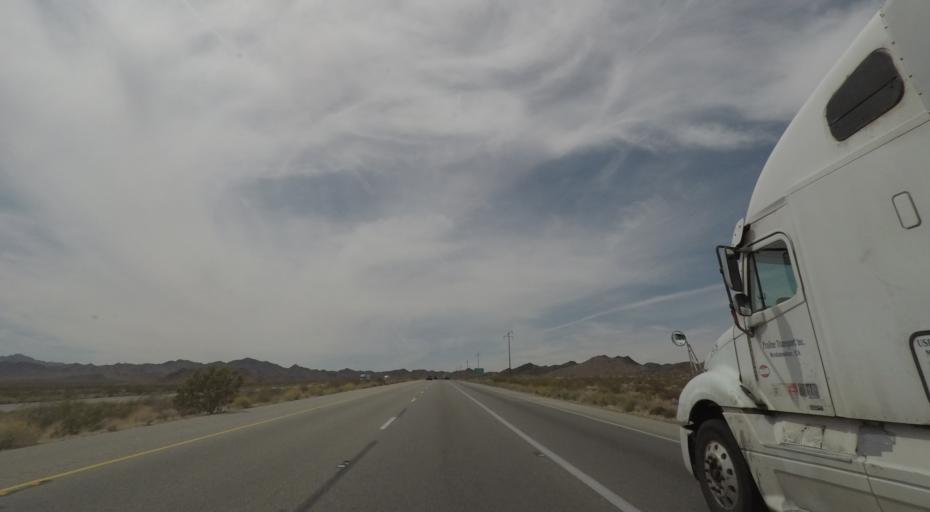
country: US
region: California
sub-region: San Bernardino County
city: Needles
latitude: 34.8337
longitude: -115.0123
